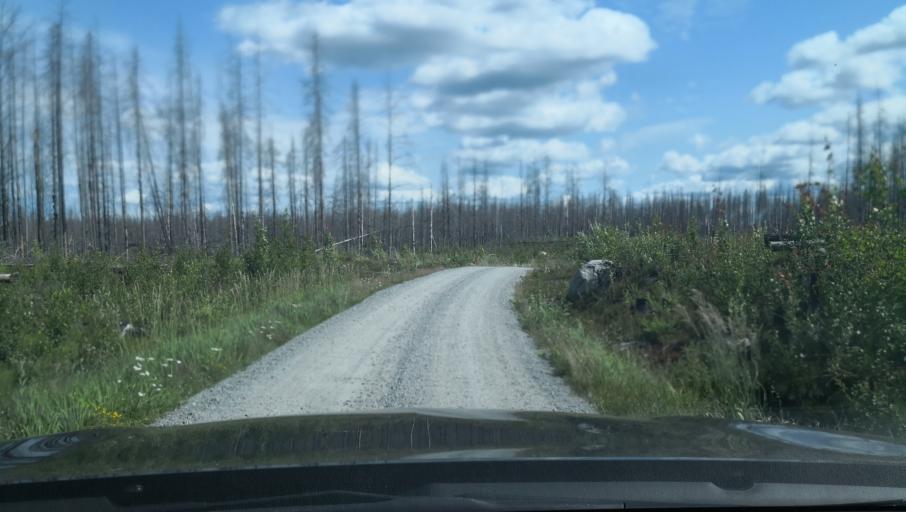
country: SE
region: Vaestmanland
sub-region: Surahammars Kommun
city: Ramnas
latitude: 59.8988
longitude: 16.1336
